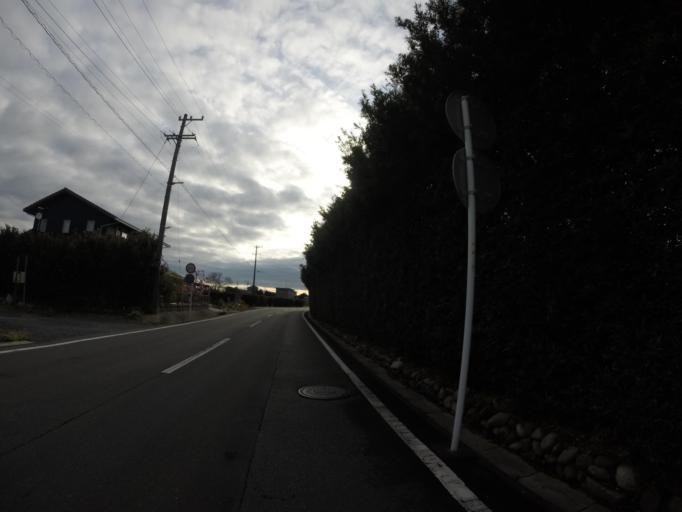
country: JP
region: Shizuoka
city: Hamakita
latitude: 34.8189
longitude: 137.7702
